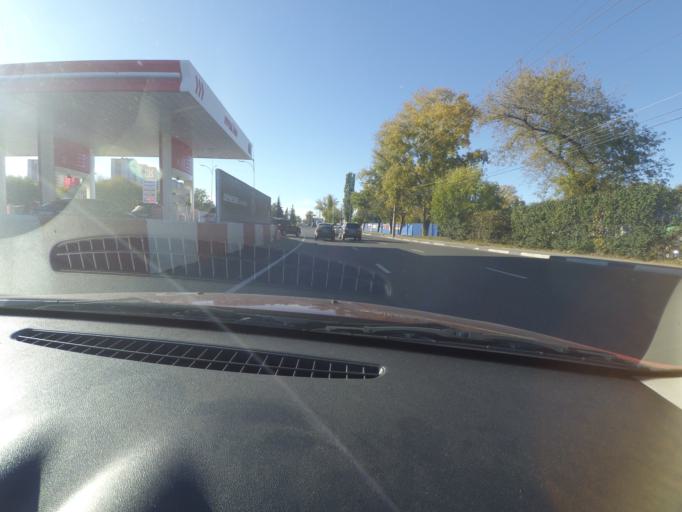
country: RU
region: Nizjnij Novgorod
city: Bor
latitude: 56.3166
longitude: 44.0692
